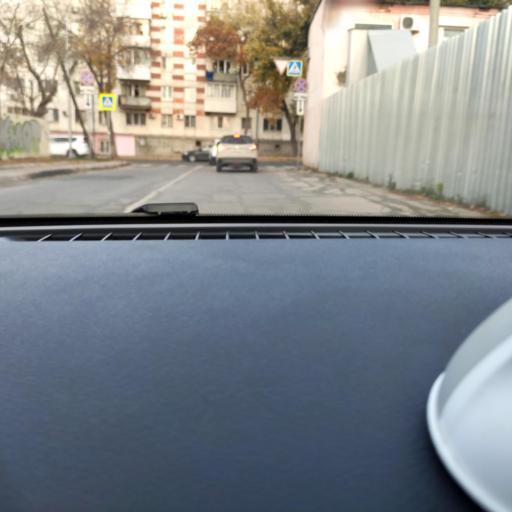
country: RU
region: Samara
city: Samara
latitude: 53.1919
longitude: 50.1316
